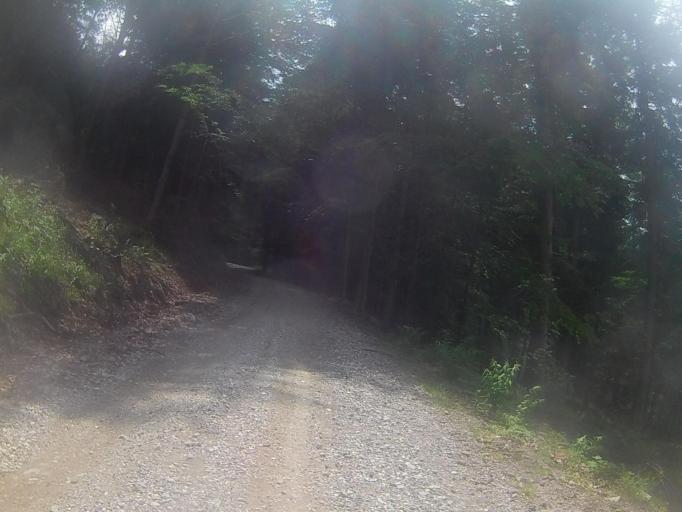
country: SI
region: Ruse
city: Bistrica ob Dravi
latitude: 46.5149
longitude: 15.5523
